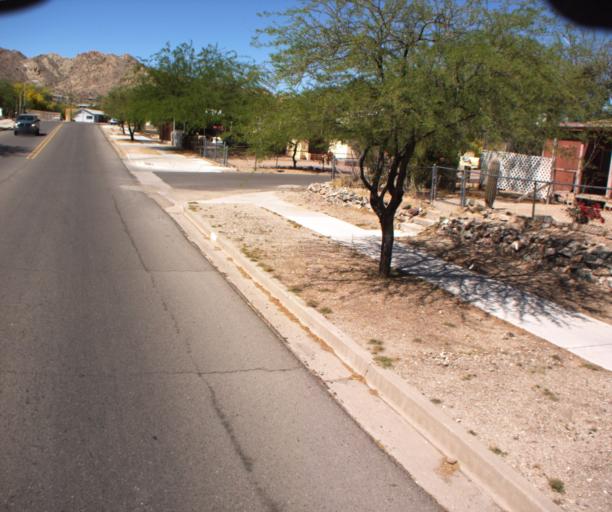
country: US
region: Arizona
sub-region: Pima County
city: Ajo
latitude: 32.3748
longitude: -112.8699
